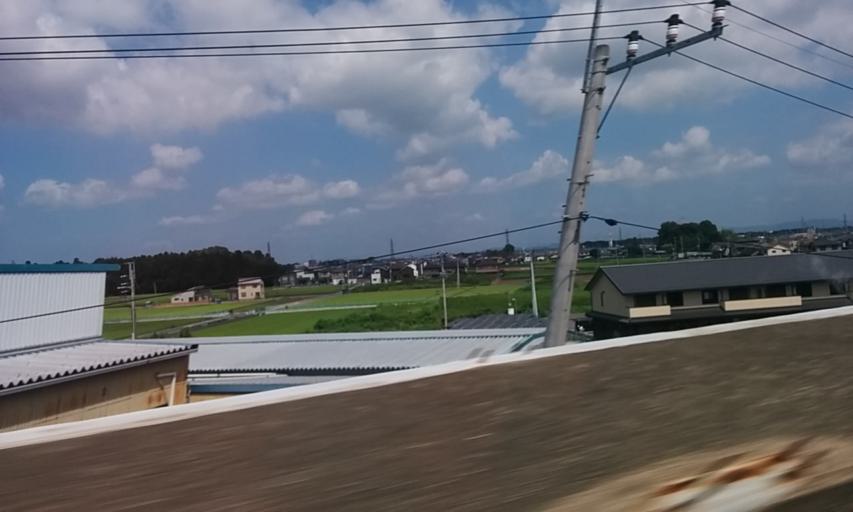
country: JP
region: Ibaraki
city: Koga
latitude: 36.1837
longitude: 139.7409
